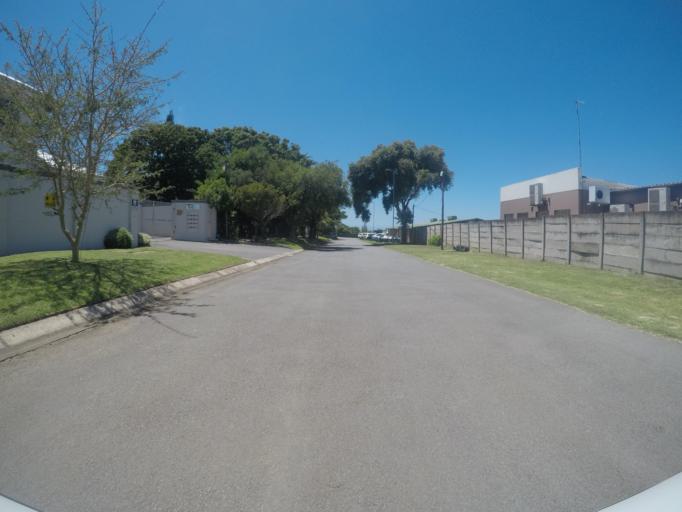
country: ZA
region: Eastern Cape
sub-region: Buffalo City Metropolitan Municipality
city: East London
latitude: -32.9352
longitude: 27.9997
